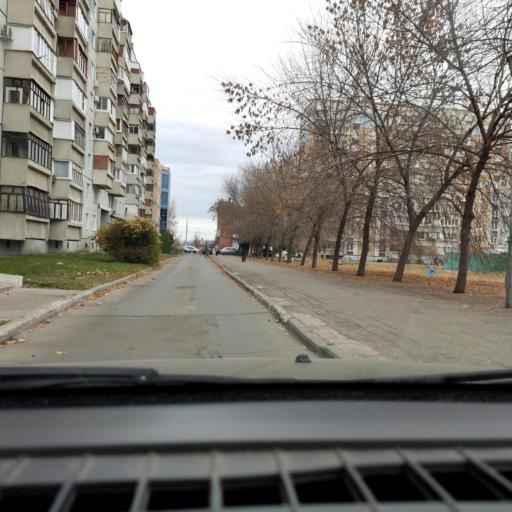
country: RU
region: Samara
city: Tol'yatti
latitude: 53.5455
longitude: 49.3569
